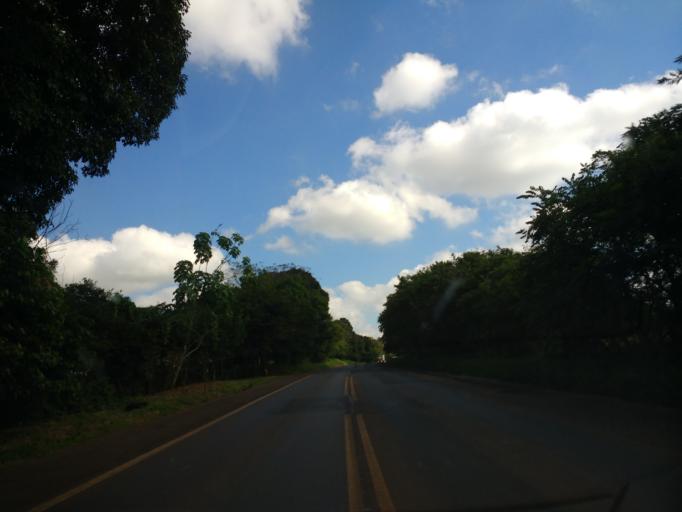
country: BR
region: Parana
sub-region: Umuarama
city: Umuarama
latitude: -23.8846
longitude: -53.3996
